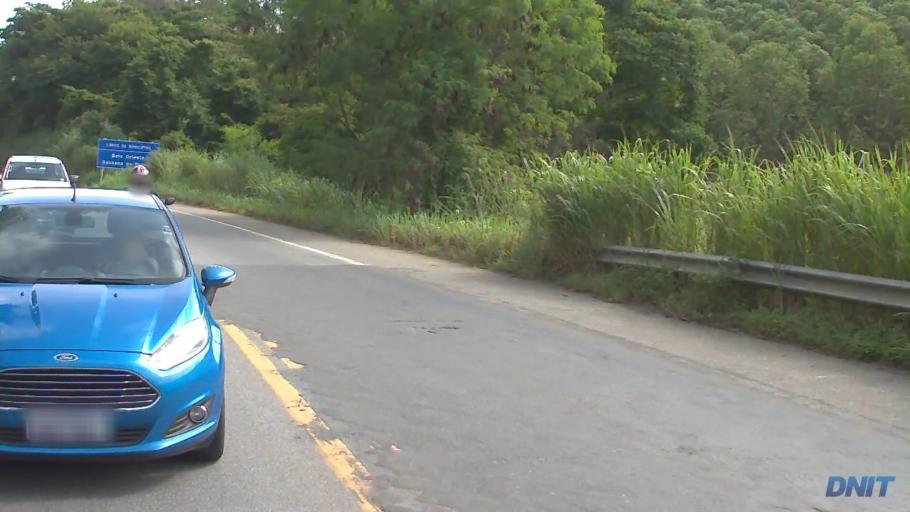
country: BR
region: Minas Gerais
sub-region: Ipaba
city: Ipaba
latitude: -19.3602
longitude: -42.4438
